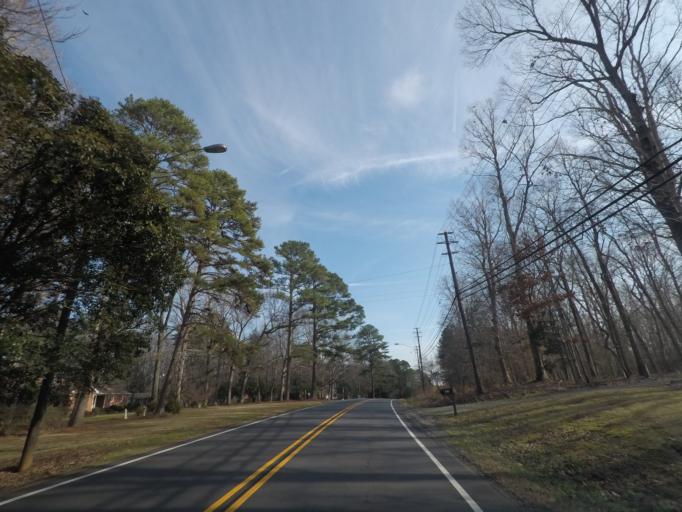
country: US
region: North Carolina
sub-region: Durham County
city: Durham
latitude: 36.0797
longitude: -78.9265
